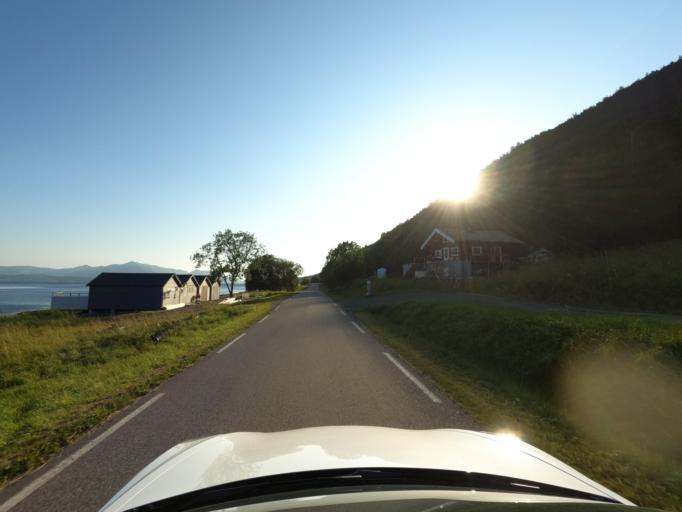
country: NO
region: Nordland
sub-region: Ballangen
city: Ballangen
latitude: 68.4617
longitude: 16.7648
